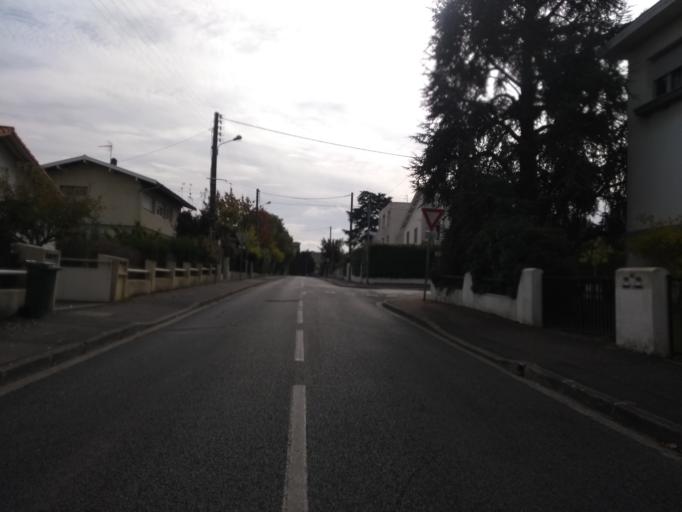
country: FR
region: Aquitaine
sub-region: Departement de la Gironde
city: Talence
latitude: 44.8127
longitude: -0.5976
